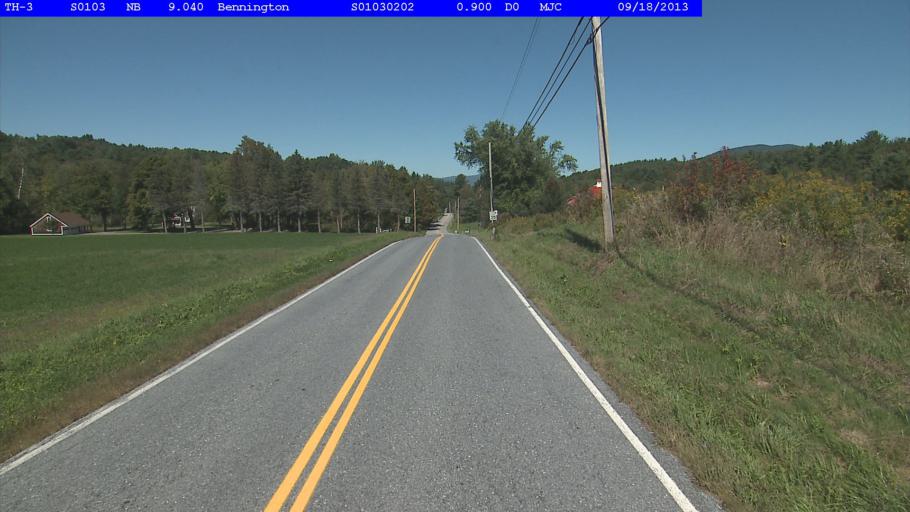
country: US
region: Vermont
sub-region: Bennington County
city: Bennington
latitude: 42.8496
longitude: -73.1725
